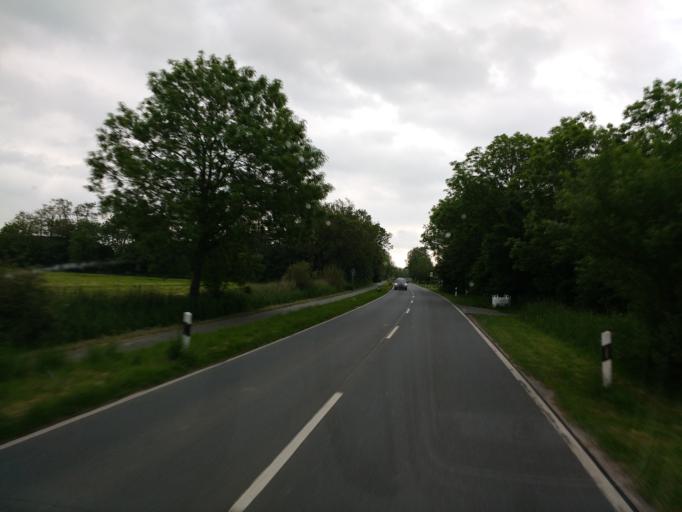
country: DE
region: Lower Saxony
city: Schillig
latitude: 53.6541
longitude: 7.9914
